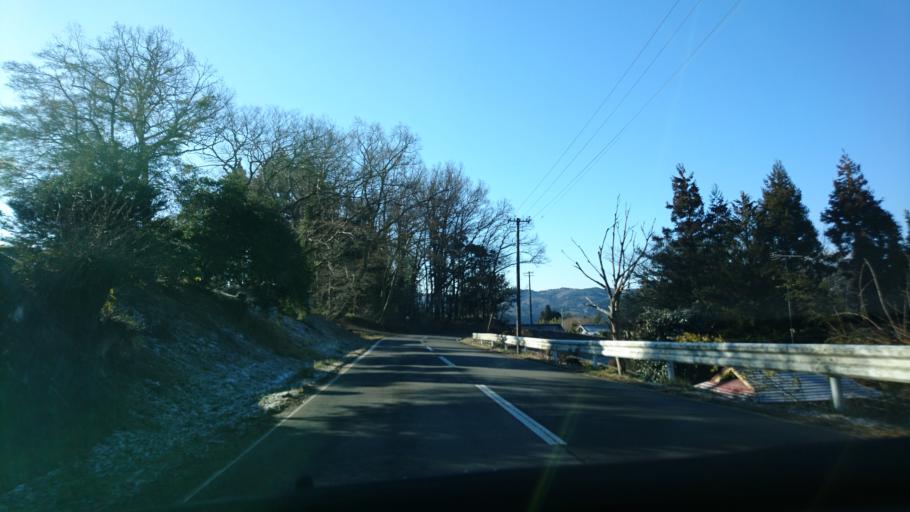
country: JP
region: Iwate
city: Ichinoseki
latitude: 38.8609
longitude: 141.2993
